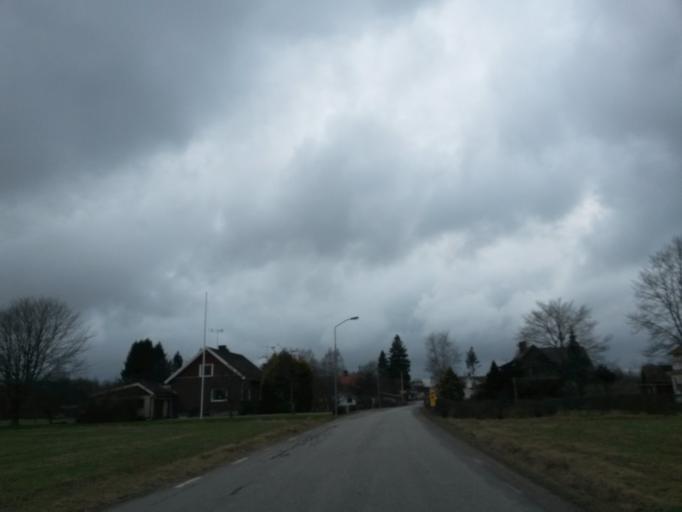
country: SE
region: Vaestra Goetaland
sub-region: Herrljunga Kommun
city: Herrljunga
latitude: 58.0844
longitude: 13.0306
